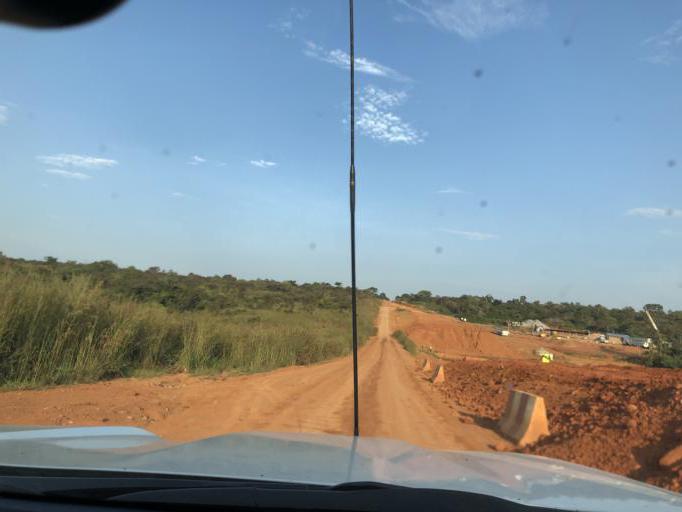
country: CF
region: Nana-Mambere
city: Bouar
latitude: 5.8945
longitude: 15.7584
